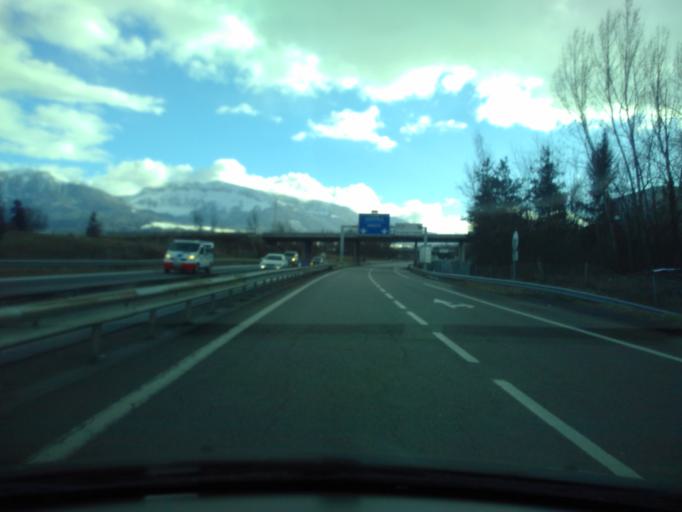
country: FR
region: Rhone-Alpes
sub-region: Departement de la Haute-Savoie
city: Etaux
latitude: 46.0761
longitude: 6.2906
